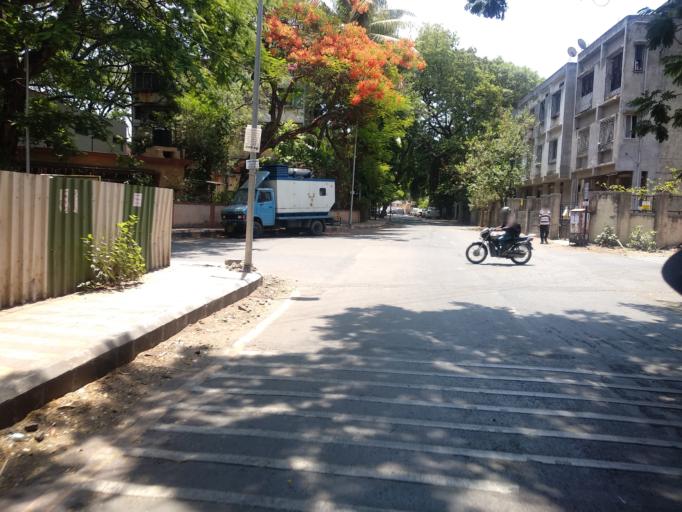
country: IN
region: Maharashtra
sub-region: Pune Division
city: Pune
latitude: 18.5046
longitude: 73.8459
